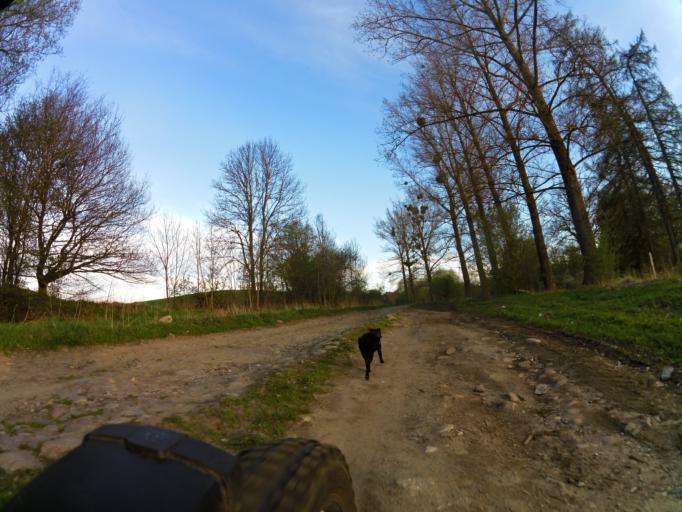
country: PL
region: West Pomeranian Voivodeship
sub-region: Powiat lobeski
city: Lobez
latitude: 53.7031
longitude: 15.6457
